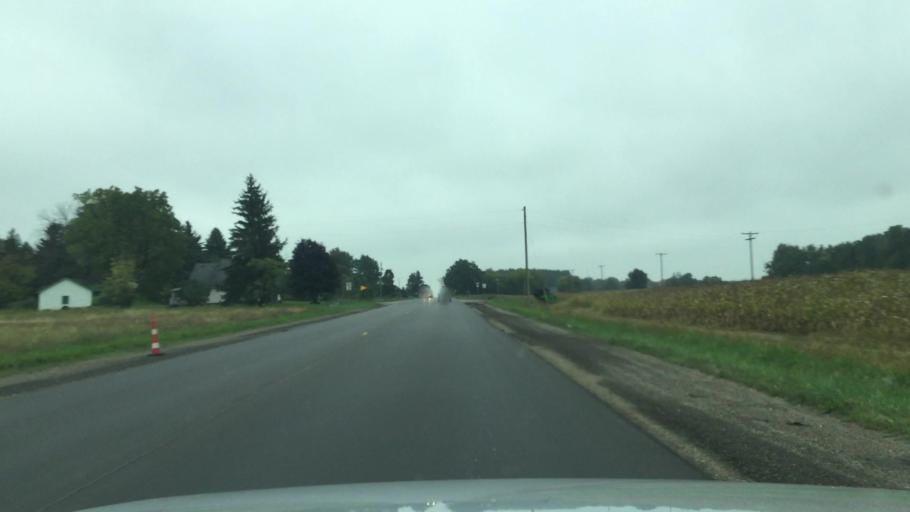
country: US
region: Michigan
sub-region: Shiawassee County
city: Perry
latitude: 42.8571
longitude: -84.2207
